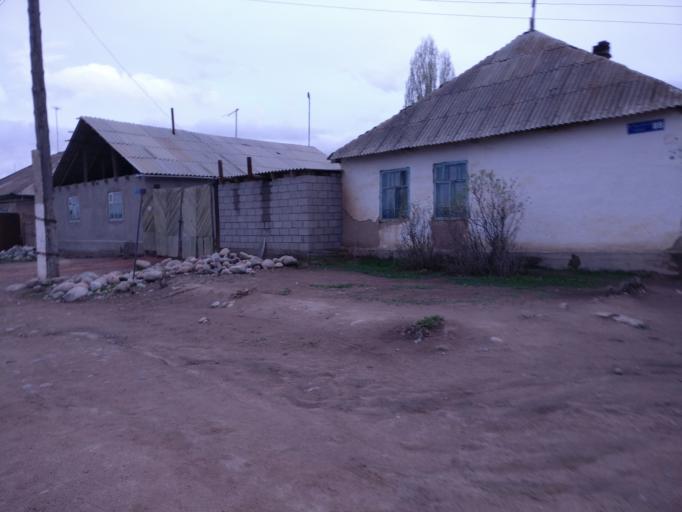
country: KG
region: Ysyk-Koel
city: Bokombayevskoye
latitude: 42.1163
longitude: 76.9887
